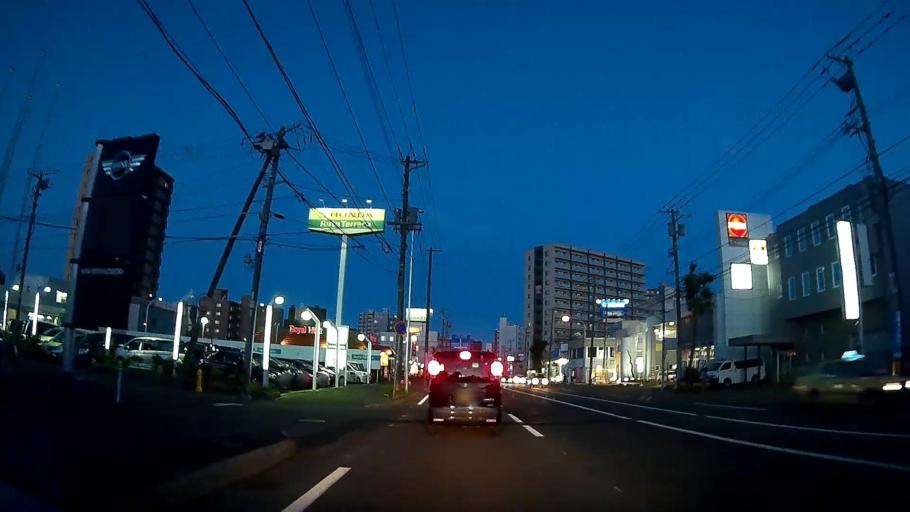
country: JP
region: Hokkaido
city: Sapporo
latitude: 43.0657
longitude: 141.3128
